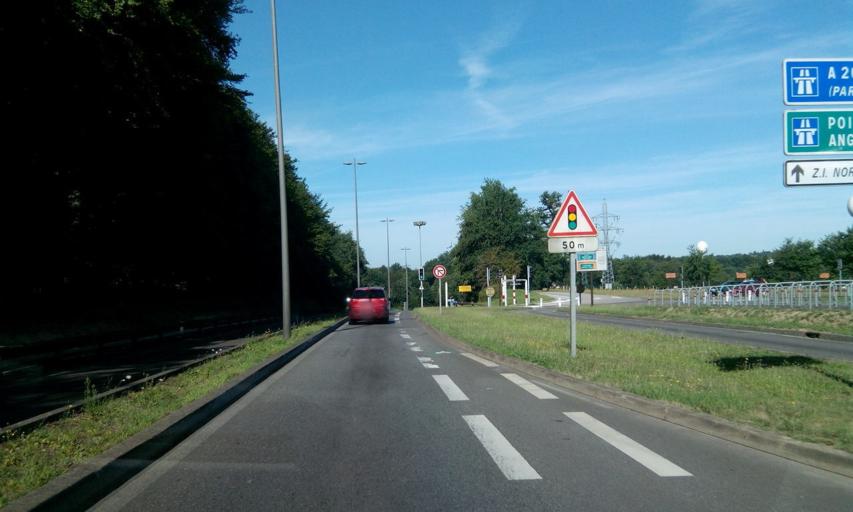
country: FR
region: Limousin
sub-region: Departement de la Haute-Vienne
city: Limoges
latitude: 45.8614
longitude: 1.2786
